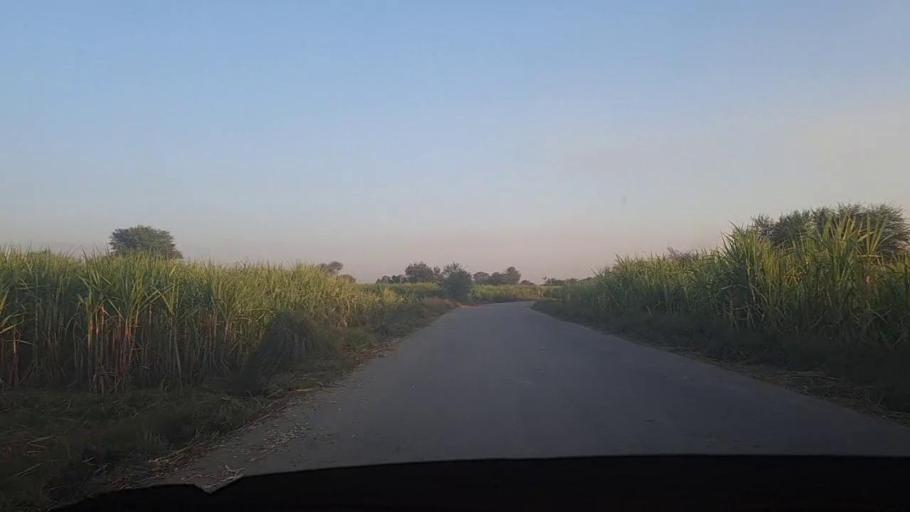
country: PK
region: Sindh
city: Sobhadero
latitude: 27.3518
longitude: 68.3744
